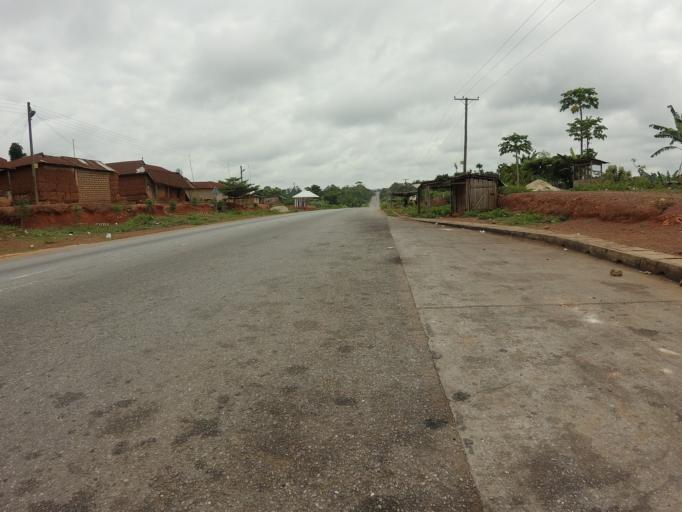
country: GH
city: Bechem
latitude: 7.0734
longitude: -1.7142
